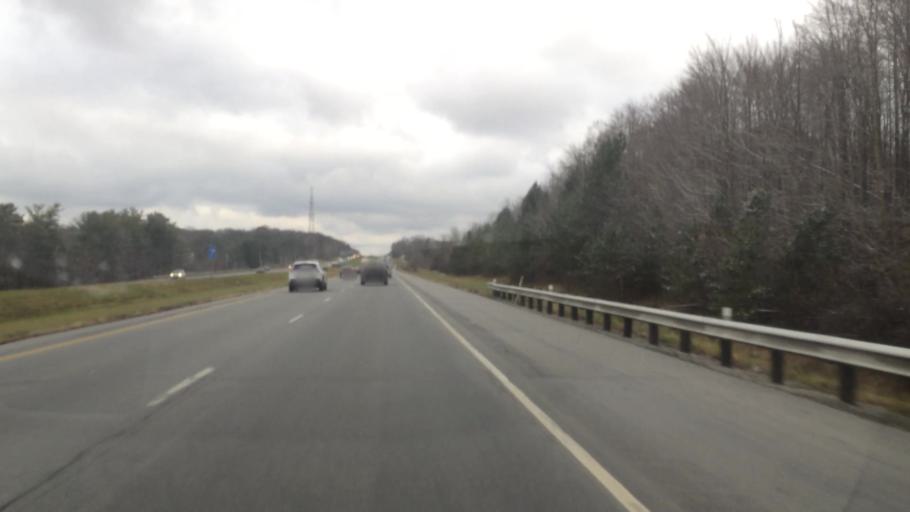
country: US
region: Ohio
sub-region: Summit County
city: Twinsburg
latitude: 41.2796
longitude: -81.4138
